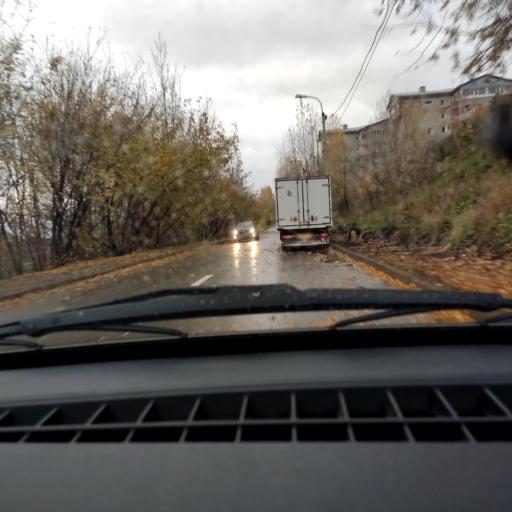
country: RU
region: Bashkortostan
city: Ufa
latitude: 54.7772
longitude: 56.0476
